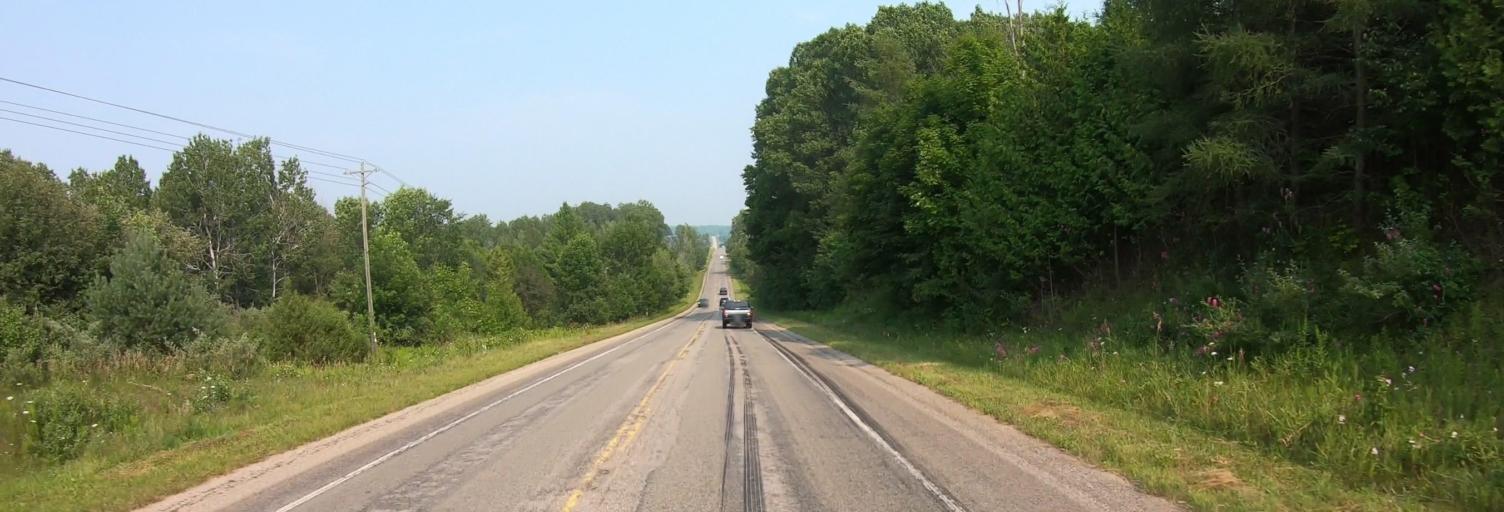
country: US
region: Michigan
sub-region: Charlevoix County
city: Charlevoix
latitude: 45.1843
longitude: -85.2746
